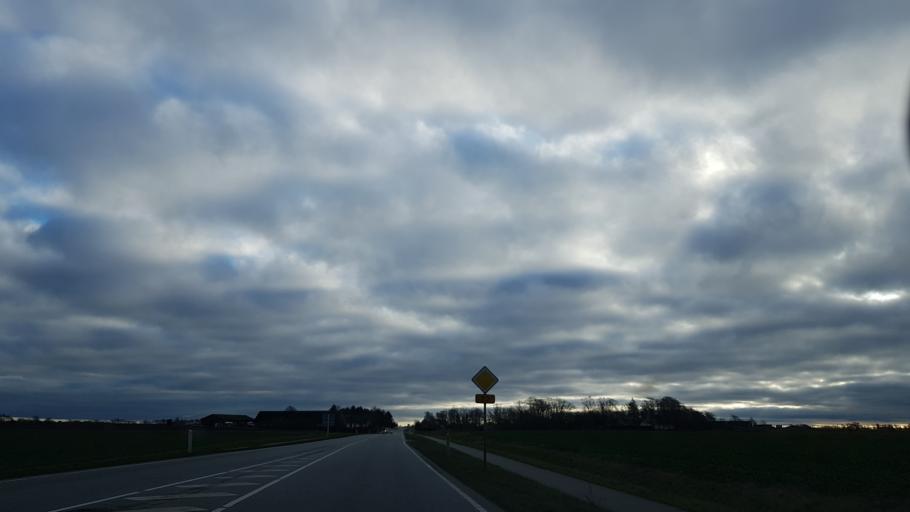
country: DK
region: Zealand
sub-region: Kalundborg Kommune
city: Gorlev
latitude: 55.5267
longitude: 11.2347
